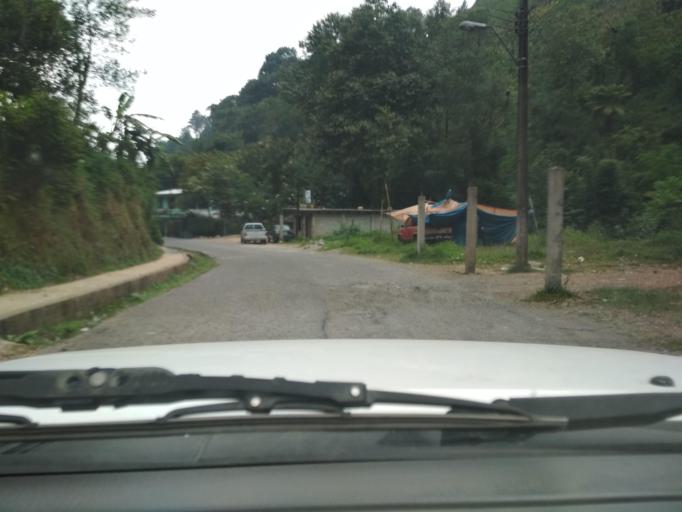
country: MX
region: Veracruz
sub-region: La Perla
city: Barrio de San Miguel
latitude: 18.9378
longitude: -97.1278
